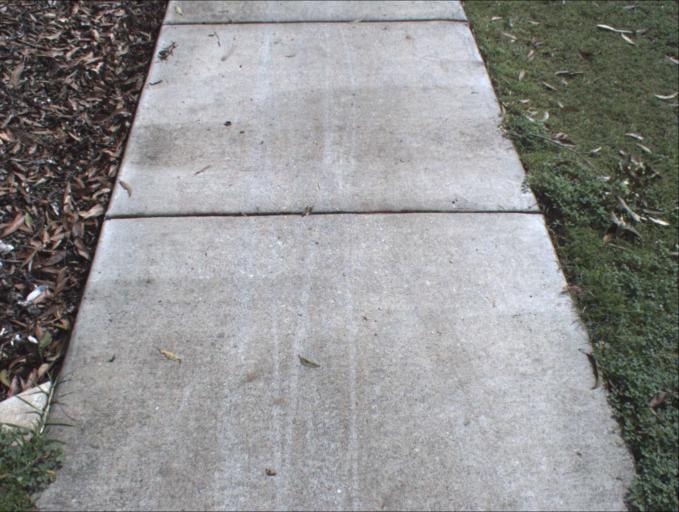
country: AU
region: Queensland
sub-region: Logan
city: Waterford West
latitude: -27.6839
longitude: 153.1165
